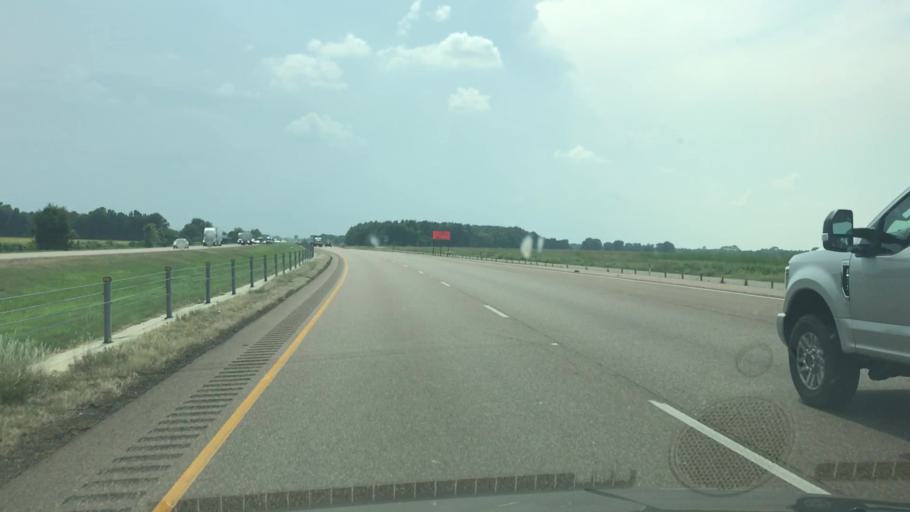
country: US
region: Arkansas
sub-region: Crittenden County
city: Earle
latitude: 35.1500
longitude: -90.4047
